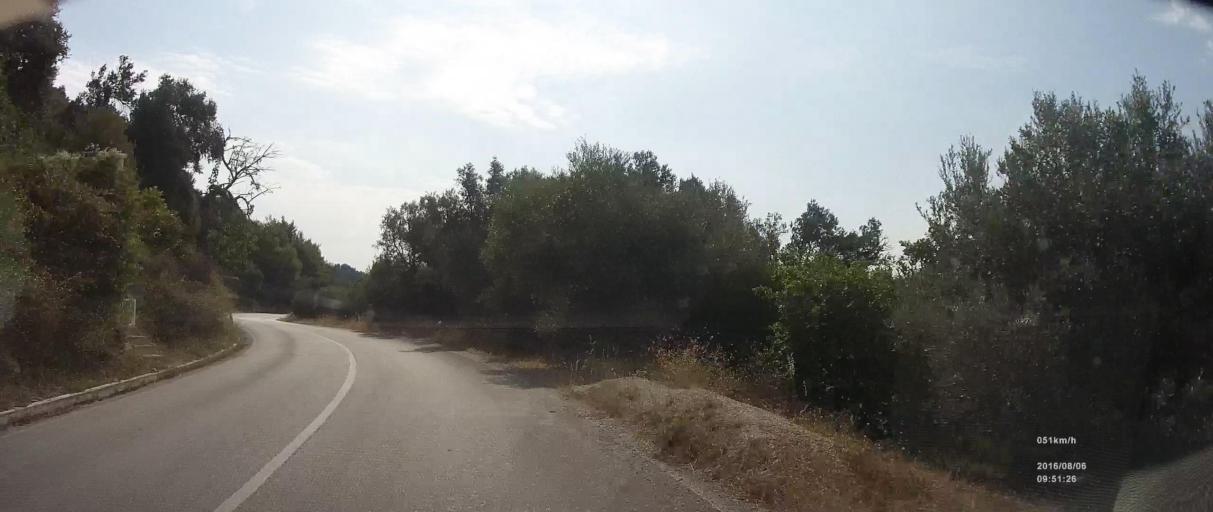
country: HR
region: Dubrovacko-Neretvanska
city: Blato
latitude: 42.7313
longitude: 17.5645
